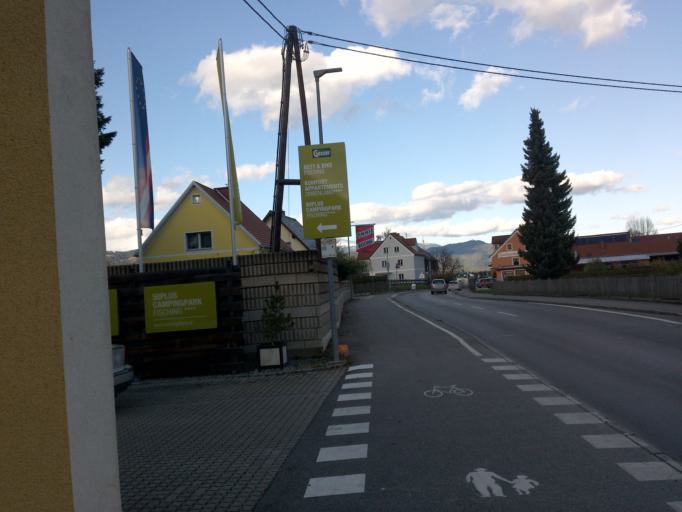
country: AT
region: Styria
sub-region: Politischer Bezirk Murtal
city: Weisskirchen in Steiermark
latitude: 47.1631
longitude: 14.7383
